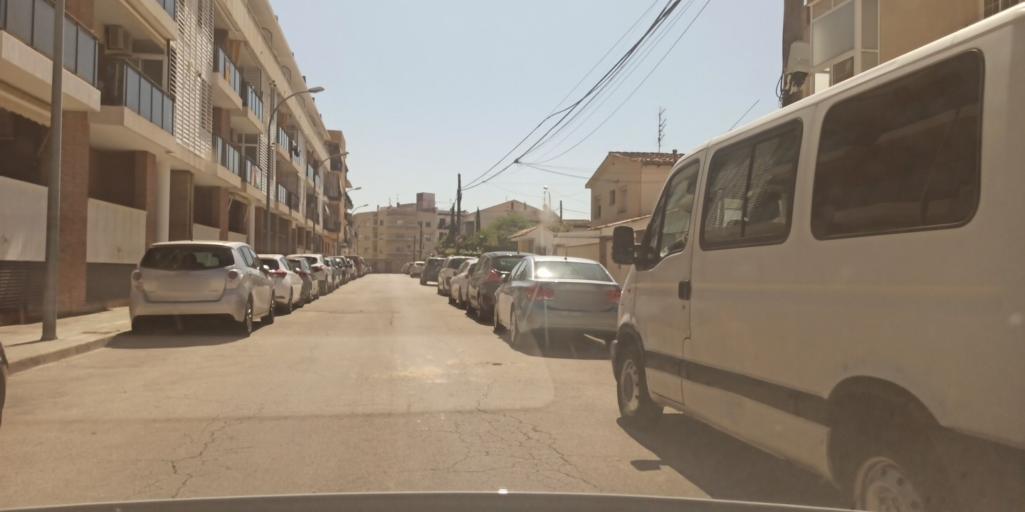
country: ES
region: Catalonia
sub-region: Provincia de Barcelona
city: Sant Pere de Ribes
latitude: 41.2579
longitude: 1.7698
